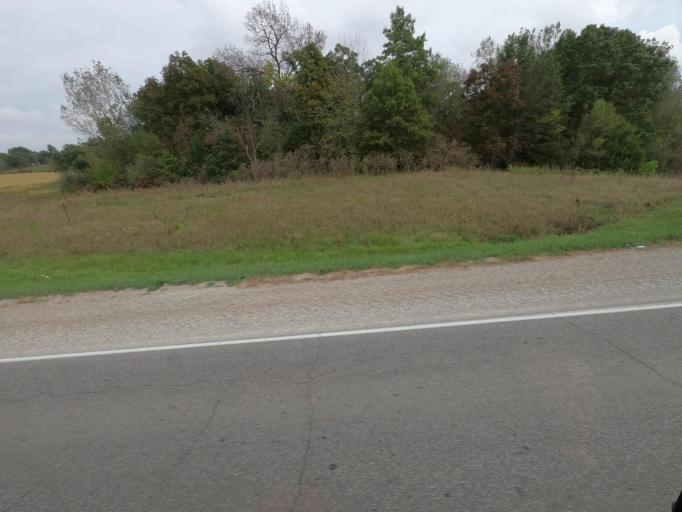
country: US
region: Iowa
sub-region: Wapello County
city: Ottumwa
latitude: 40.9248
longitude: -92.2305
